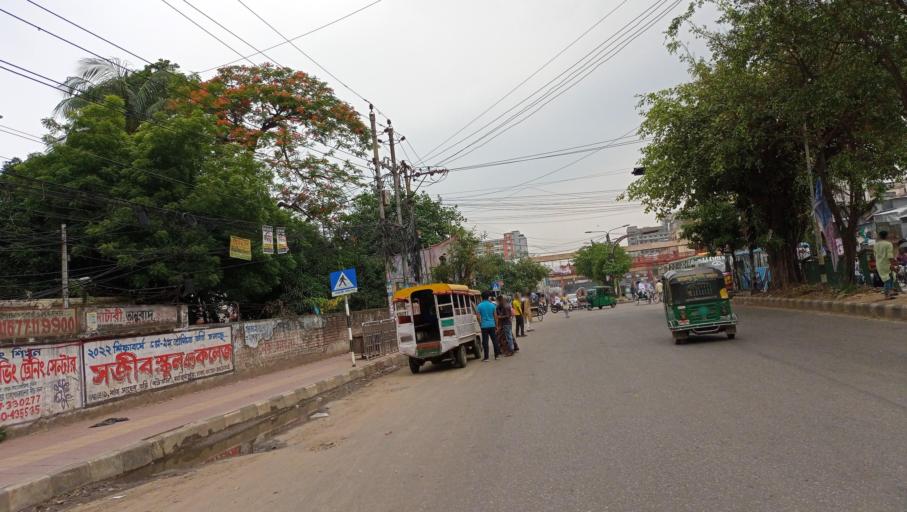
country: BD
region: Dhaka
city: Azimpur
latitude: 23.7319
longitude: 90.3852
